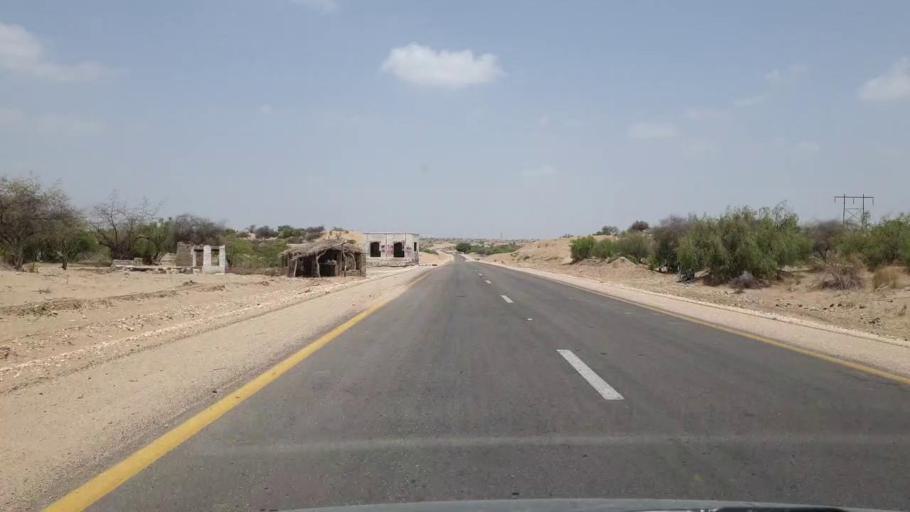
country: PK
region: Sindh
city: Mithi
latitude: 24.8055
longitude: 69.7229
